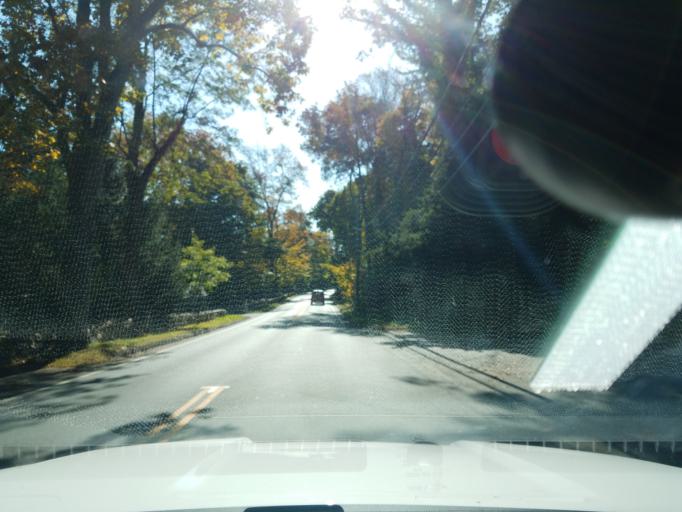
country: US
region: Connecticut
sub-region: Fairfield County
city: Cos Cob
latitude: 41.0846
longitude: -73.6262
